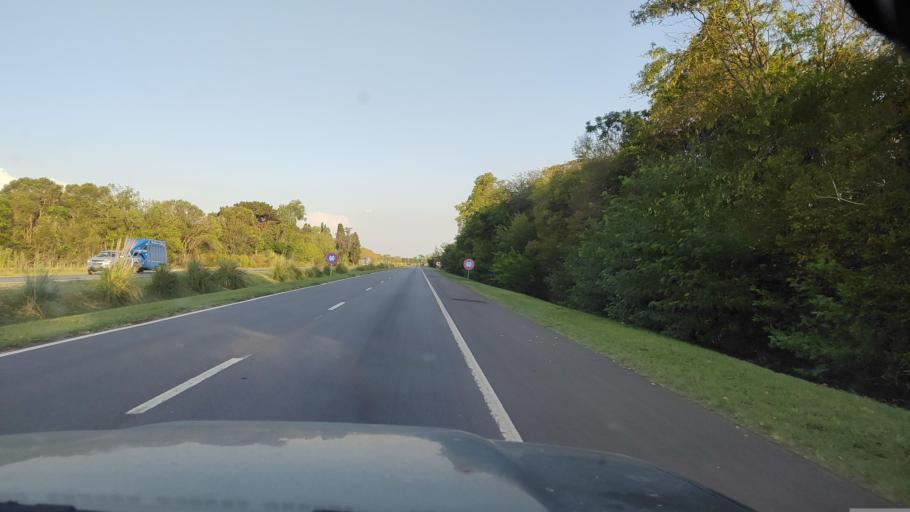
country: AR
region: Buenos Aires
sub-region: Partido de Lujan
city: Lujan
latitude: -34.5466
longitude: -59.2078
